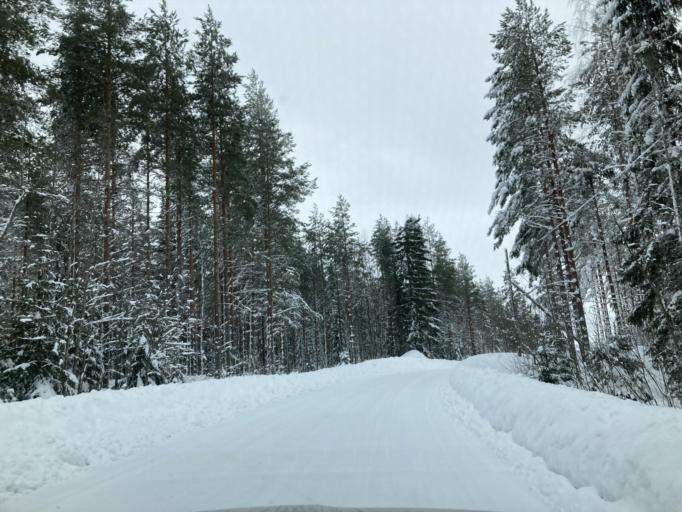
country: FI
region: Central Finland
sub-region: Jaemsae
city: Jaemsae
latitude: 61.8769
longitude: 25.3206
